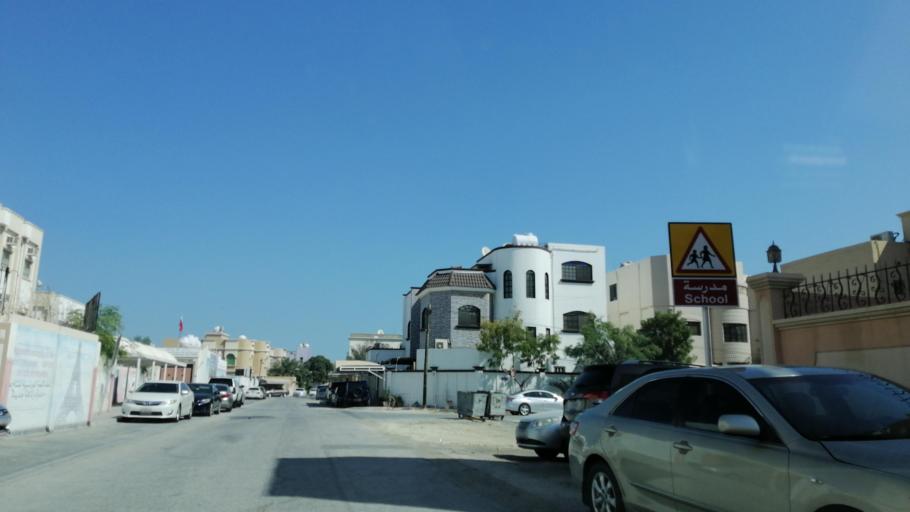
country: BH
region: Muharraq
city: Al Hadd
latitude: 26.2490
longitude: 50.6365
